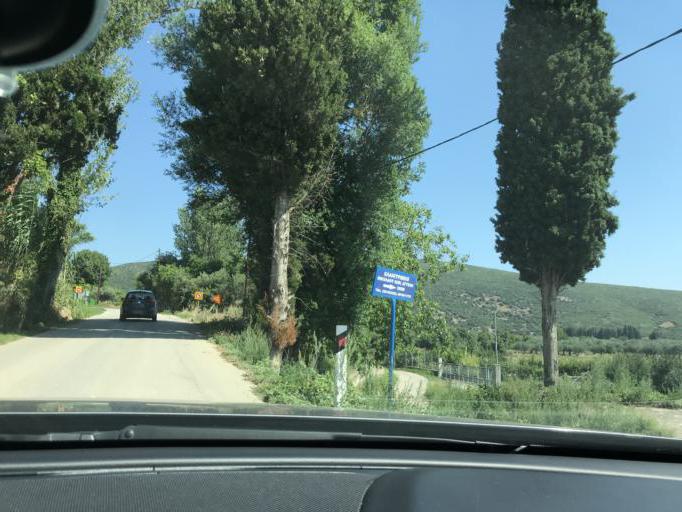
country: GR
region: Central Greece
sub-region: Nomos Fthiotidos
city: Kato Tithorea
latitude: 38.5174
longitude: 22.7486
